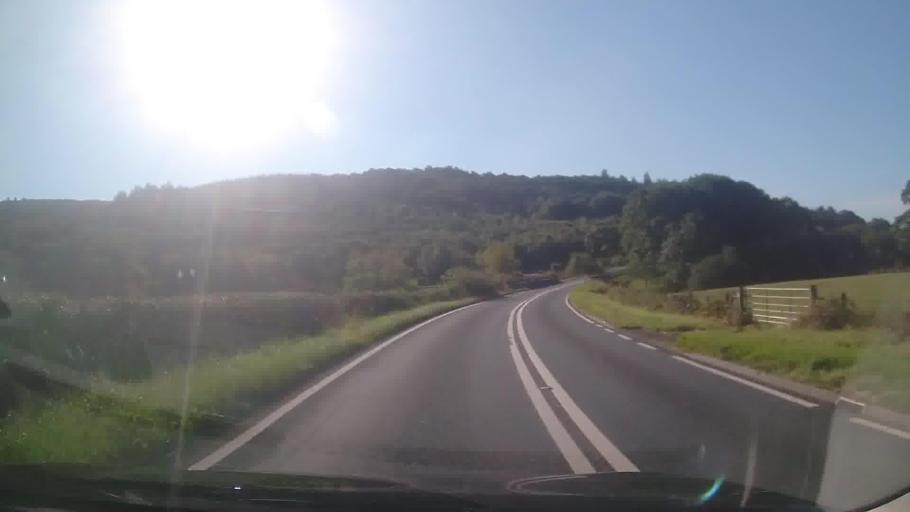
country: GB
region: England
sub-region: Cumbria
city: Seascale
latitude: 54.3677
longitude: -3.3956
